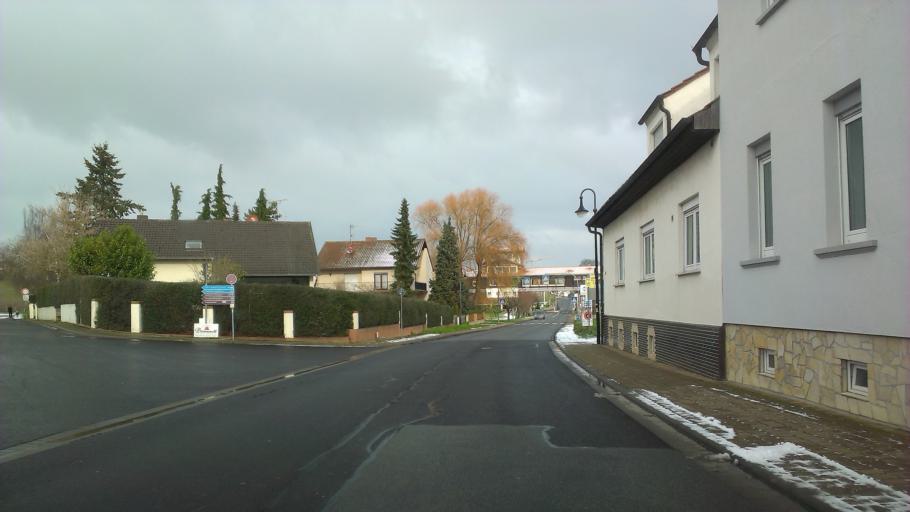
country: DE
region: Rheinland-Pfalz
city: Bockenheim
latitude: 49.6073
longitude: 8.1812
